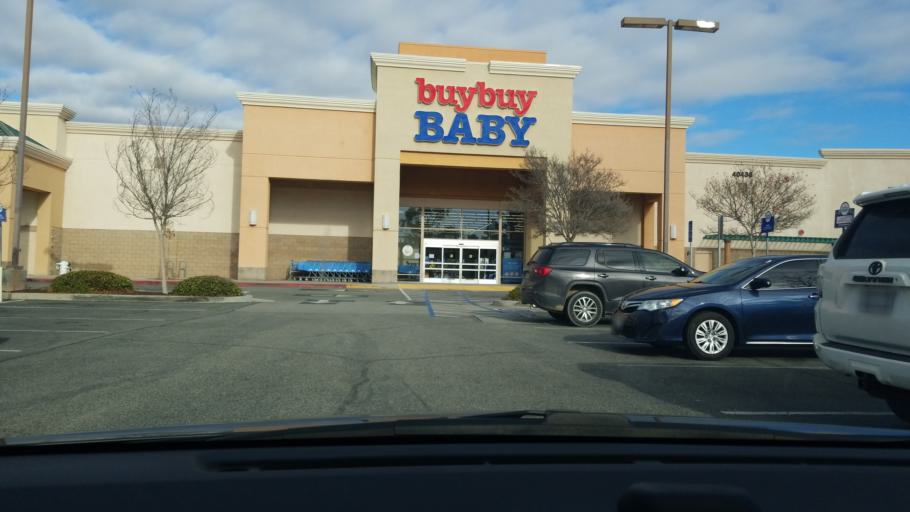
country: US
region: California
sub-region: Riverside County
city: Murrieta Hot Springs
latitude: 33.5291
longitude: -117.1514
